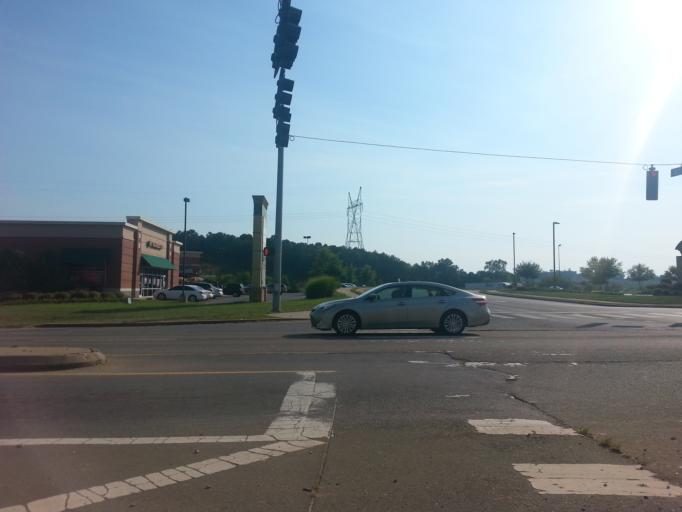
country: US
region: Tennessee
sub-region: Loudon County
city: Lenoir City
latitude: 35.8211
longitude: -84.2680
